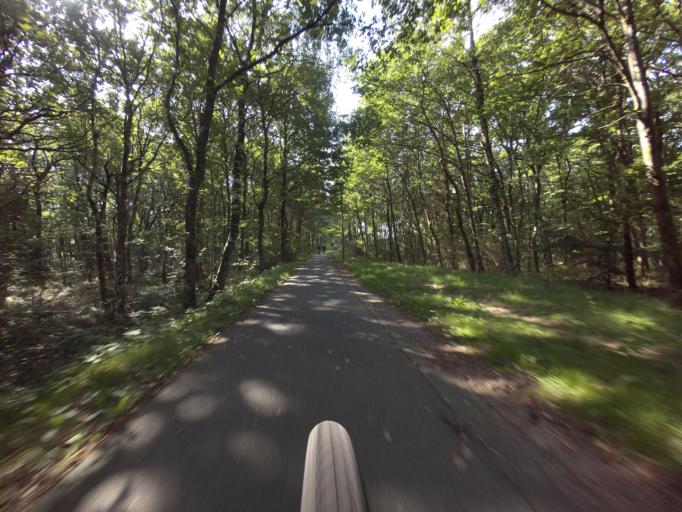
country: DK
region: Central Jutland
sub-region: Viborg Kommune
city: Viborg
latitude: 56.4032
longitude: 9.3556
